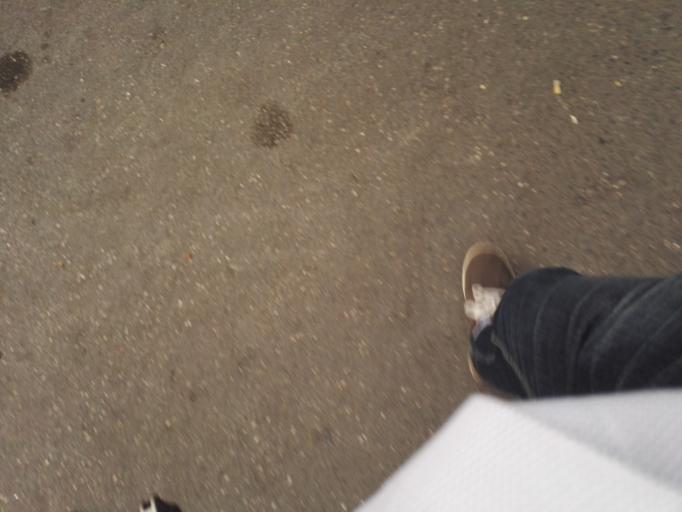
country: VN
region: Ha Noi
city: Hoan Kiem
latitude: 21.0446
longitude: 105.8499
